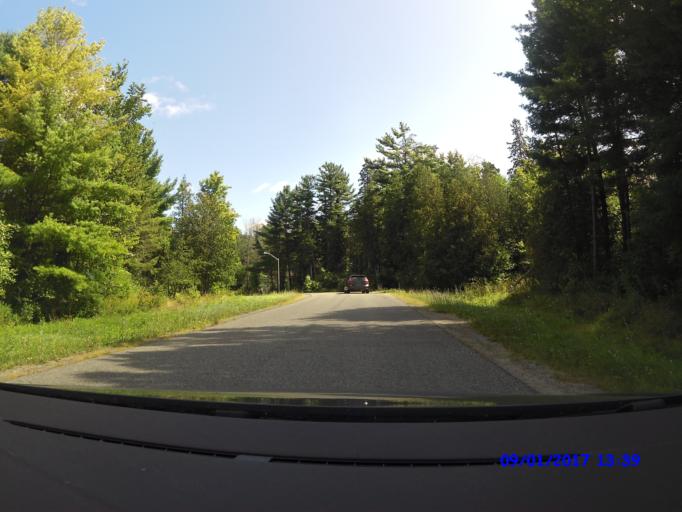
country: CA
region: Ontario
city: Bells Corners
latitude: 45.3592
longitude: -75.9758
